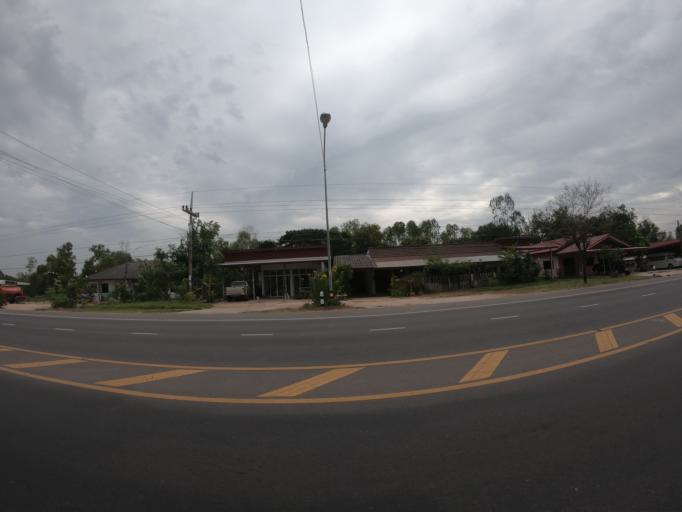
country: TH
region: Roi Et
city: Thawat Buri
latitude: 16.0828
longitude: 103.7419
